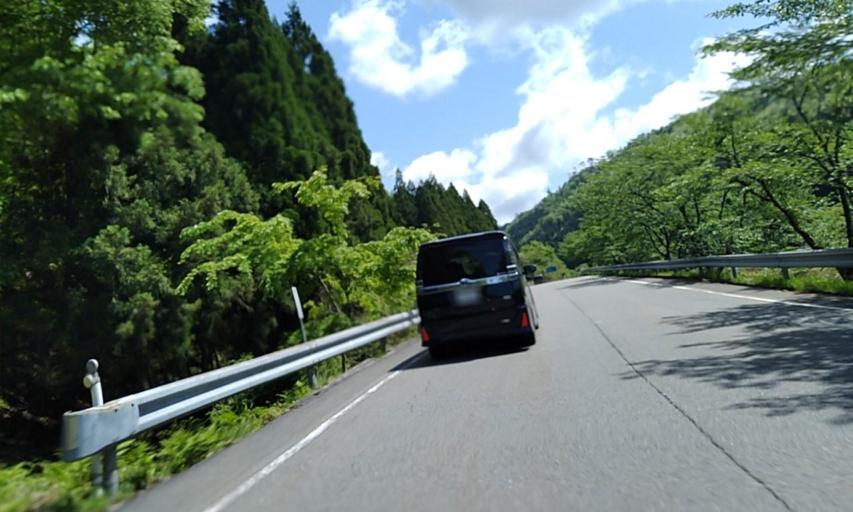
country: JP
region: Fukui
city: Obama
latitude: 35.3360
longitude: 135.5759
